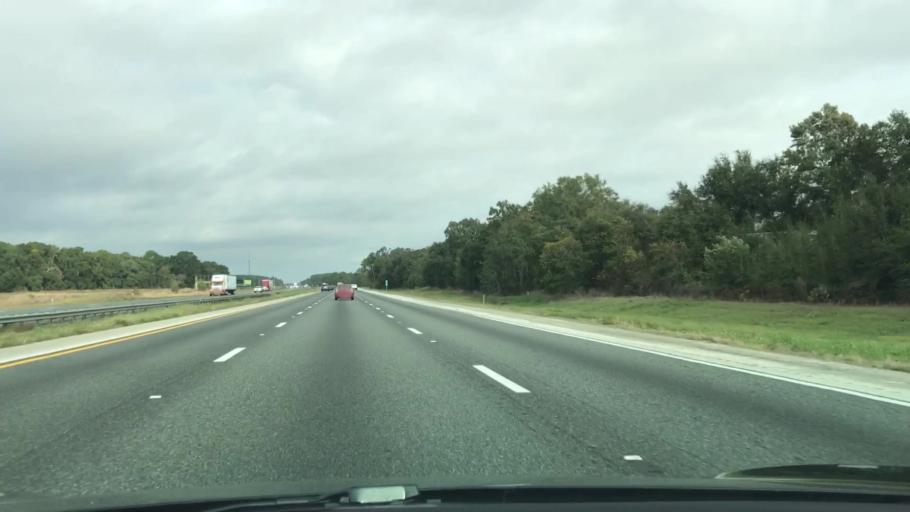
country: US
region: Florida
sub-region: Marion County
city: Belleview
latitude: 28.9610
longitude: -82.1281
